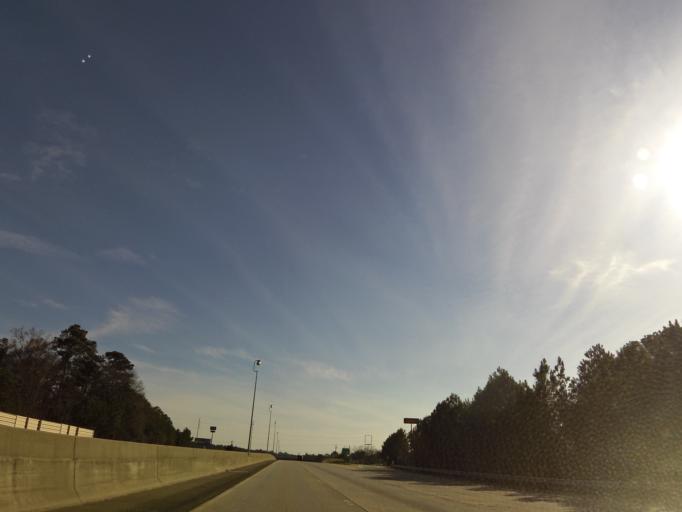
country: US
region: Georgia
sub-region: Muscogee County
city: Columbus
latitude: 32.4498
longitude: -84.9283
